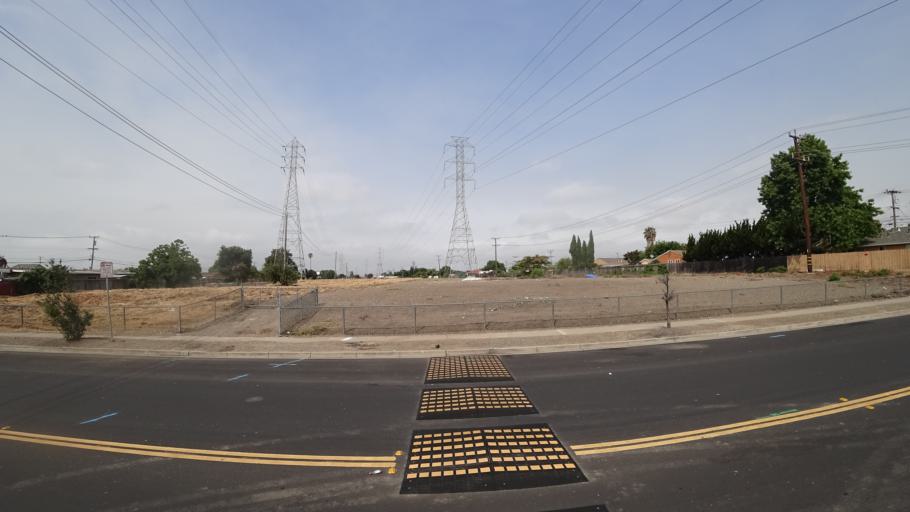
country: US
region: California
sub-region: Alameda County
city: Hayward
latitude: 37.6316
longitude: -122.1040
